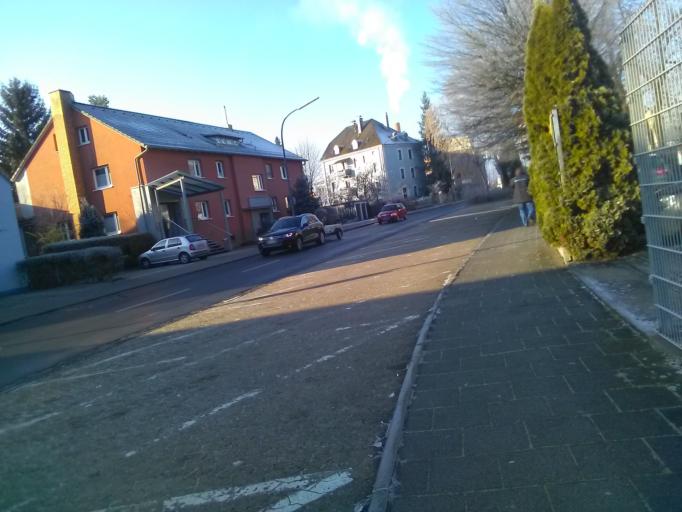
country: DE
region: Bavaria
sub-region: Upper Franconia
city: Forchheim
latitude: 49.7163
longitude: 11.0668
